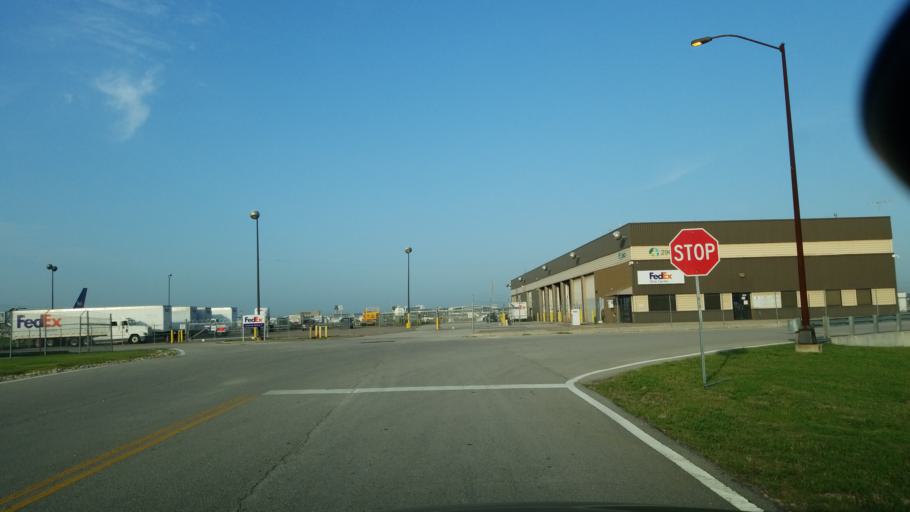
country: US
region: Texas
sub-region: Dallas County
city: Coppell
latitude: 32.9183
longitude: -97.0207
